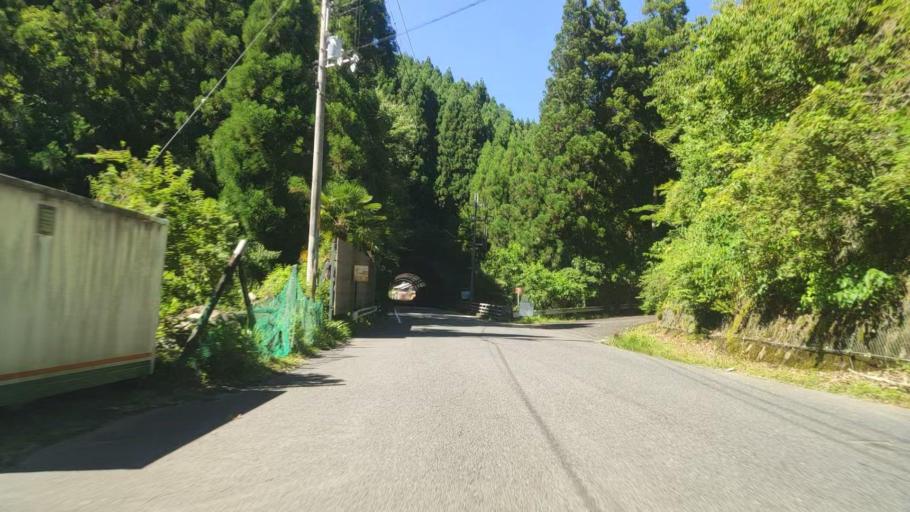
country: JP
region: Nara
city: Yoshino-cho
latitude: 34.4061
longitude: 135.9307
